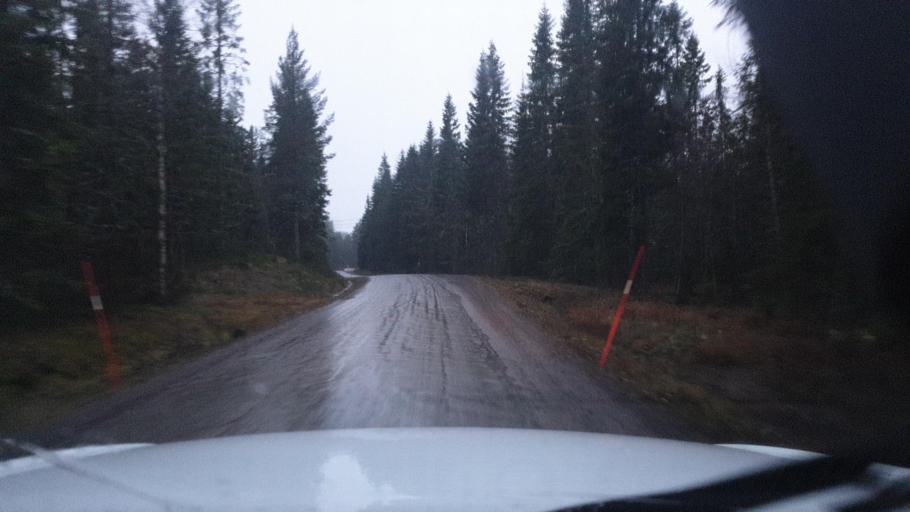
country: SE
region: Vaermland
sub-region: Sunne Kommun
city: Sunne
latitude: 59.8360
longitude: 12.9255
